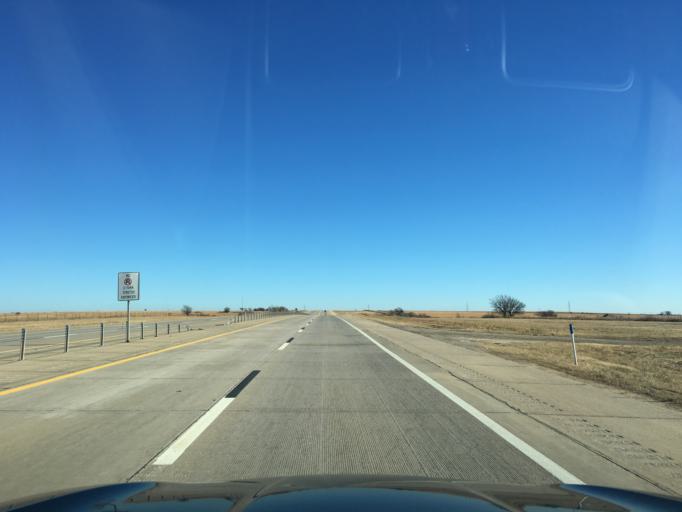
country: US
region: Oklahoma
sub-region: Noble County
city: Perry
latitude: 36.3921
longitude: -97.1311
